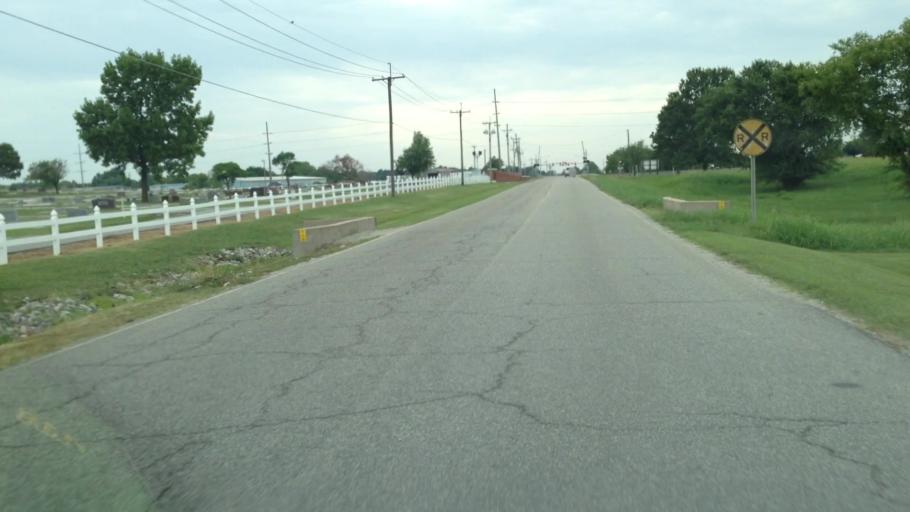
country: US
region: Oklahoma
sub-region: Craig County
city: Vinita
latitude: 36.6560
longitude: -95.1398
